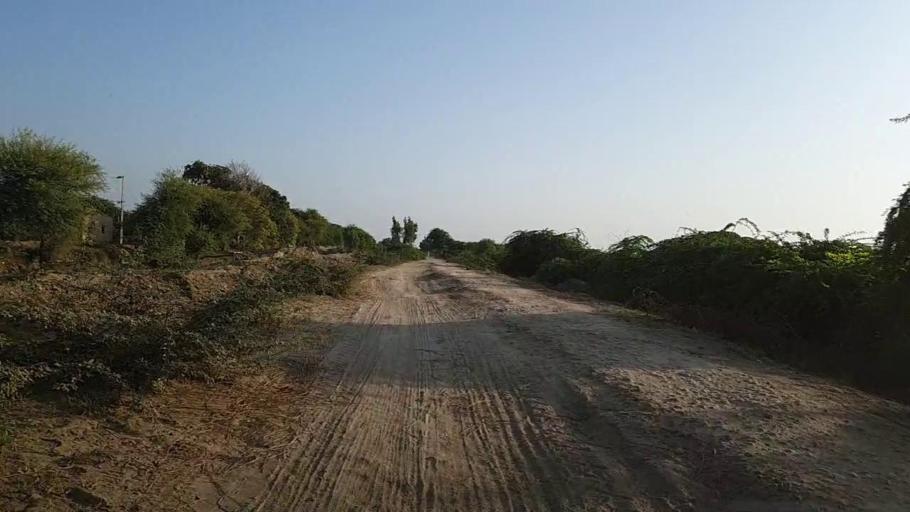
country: PK
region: Sindh
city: Kario
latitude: 24.7242
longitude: 68.6674
